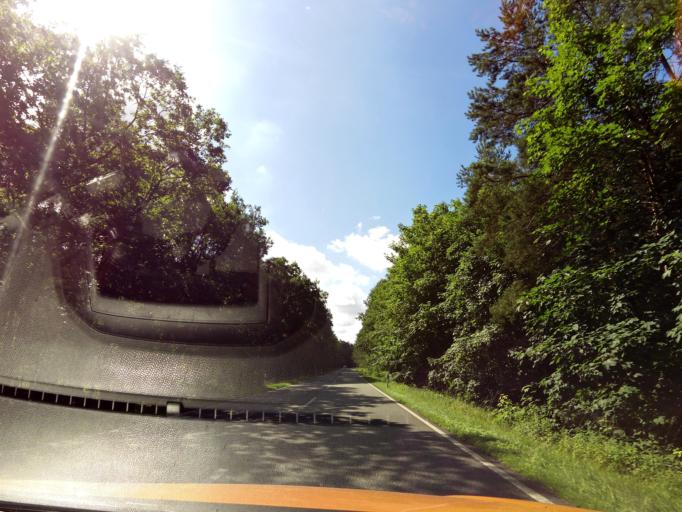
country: DE
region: Mecklenburg-Vorpommern
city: Krakow am See
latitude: 53.5641
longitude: 12.2732
